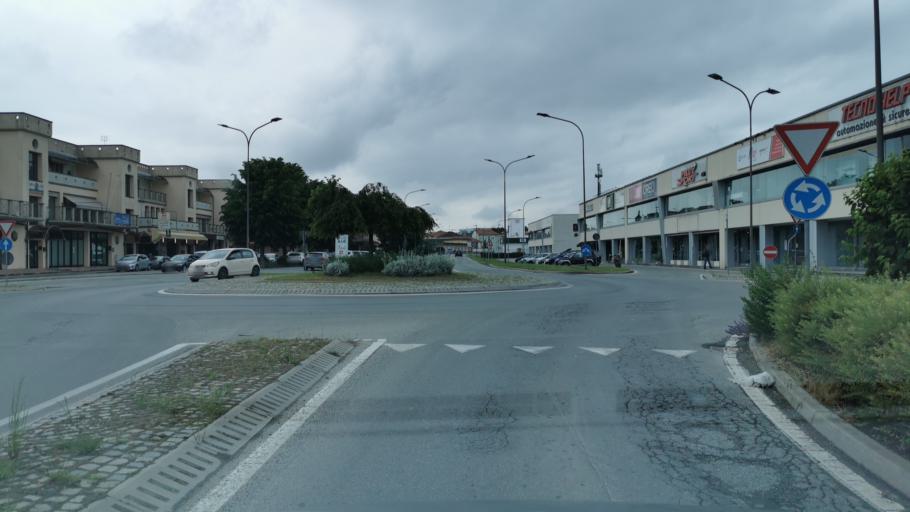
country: IT
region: Piedmont
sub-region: Provincia di Cuneo
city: Savigliano
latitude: 44.6558
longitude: 7.6552
